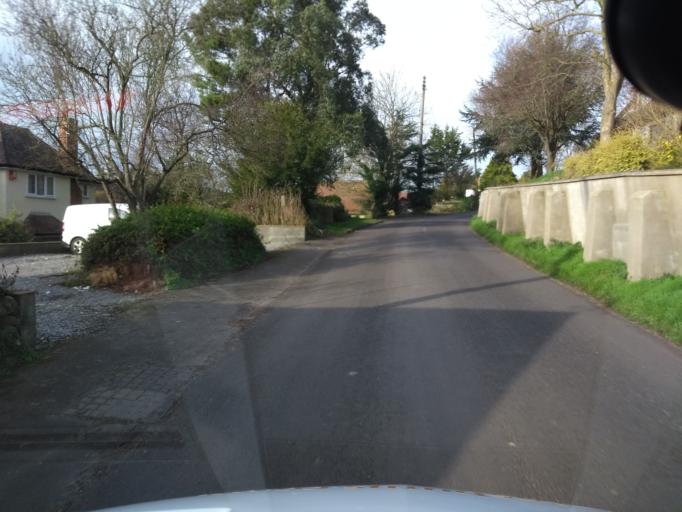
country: GB
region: England
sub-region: North Somerset
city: Bleadon
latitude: 51.3110
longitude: -2.9480
